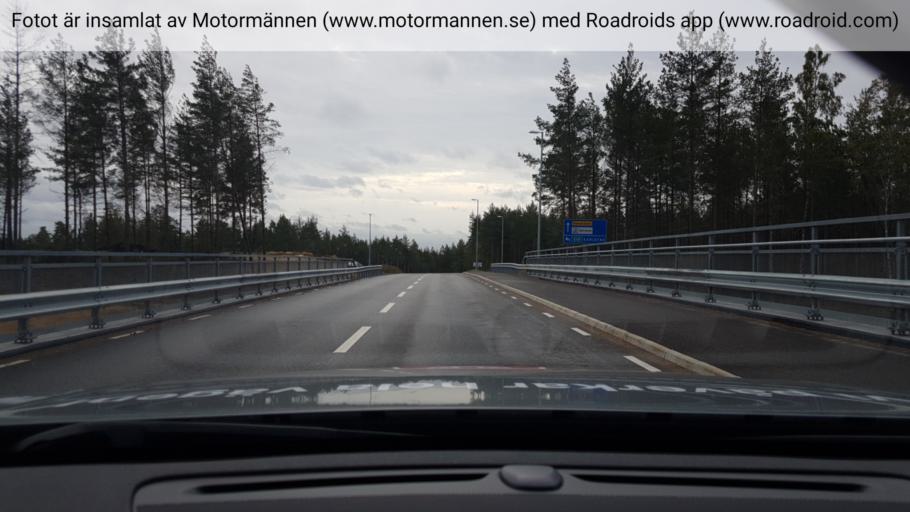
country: SE
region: Vaermland
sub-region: Kils Kommun
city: Kil
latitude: 59.3847
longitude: 13.3354
